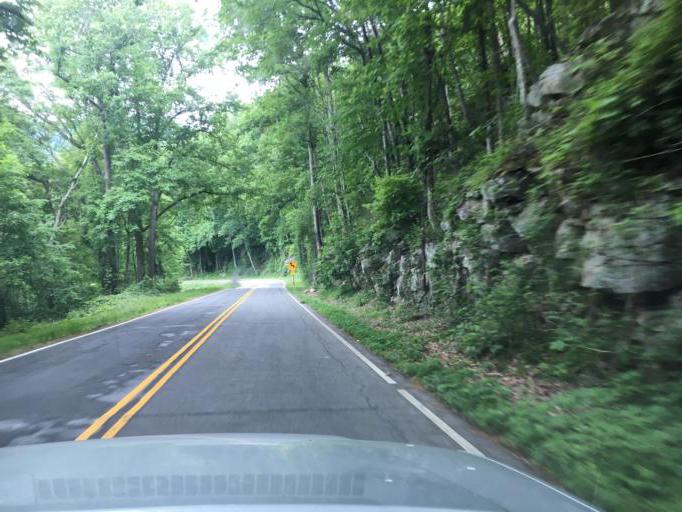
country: US
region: South Carolina
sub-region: Greenville County
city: Tigerville
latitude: 35.1650
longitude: -82.4103
